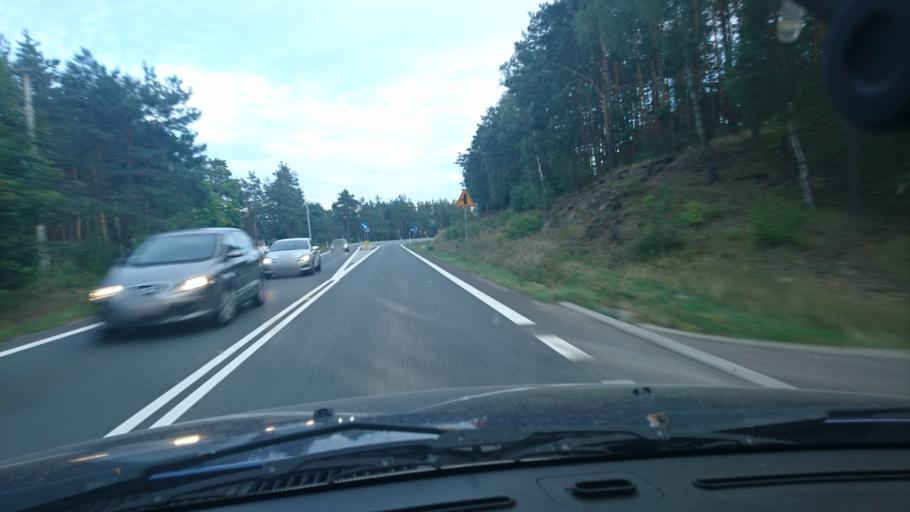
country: PL
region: Silesian Voivodeship
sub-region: Powiat tarnogorski
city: Tworog
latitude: 50.5992
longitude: 18.7022
